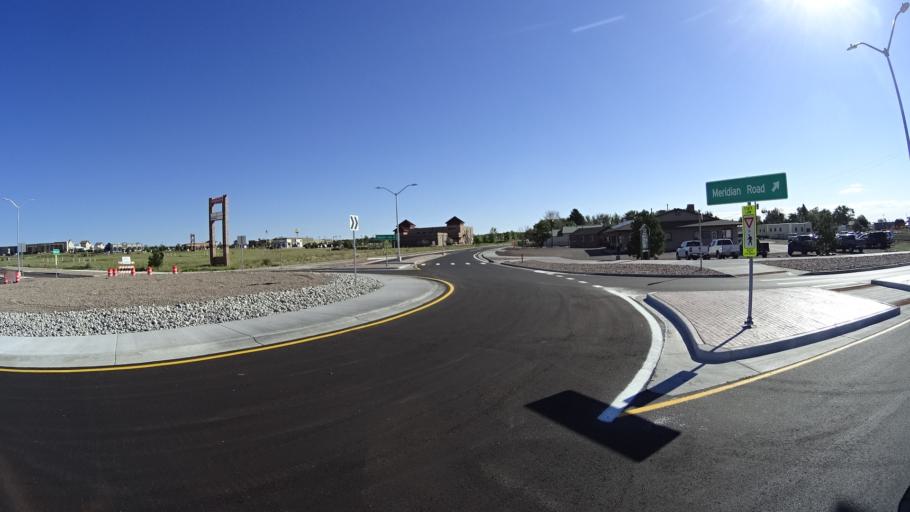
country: US
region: Colorado
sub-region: El Paso County
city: Cimarron Hills
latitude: 38.9350
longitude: -104.6108
